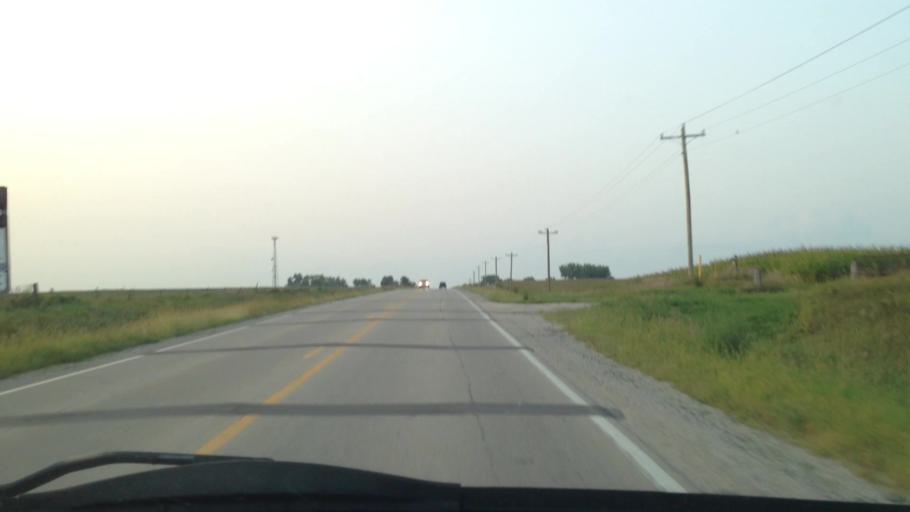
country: US
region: Iowa
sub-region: Linn County
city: Palo
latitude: 42.0724
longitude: -91.8691
